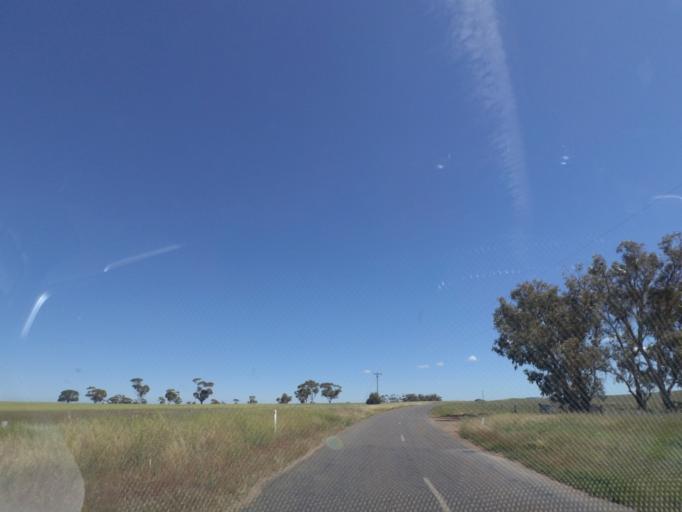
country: AU
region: Victoria
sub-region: Moorabool
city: Bacchus Marsh
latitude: -37.7951
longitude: 144.3812
